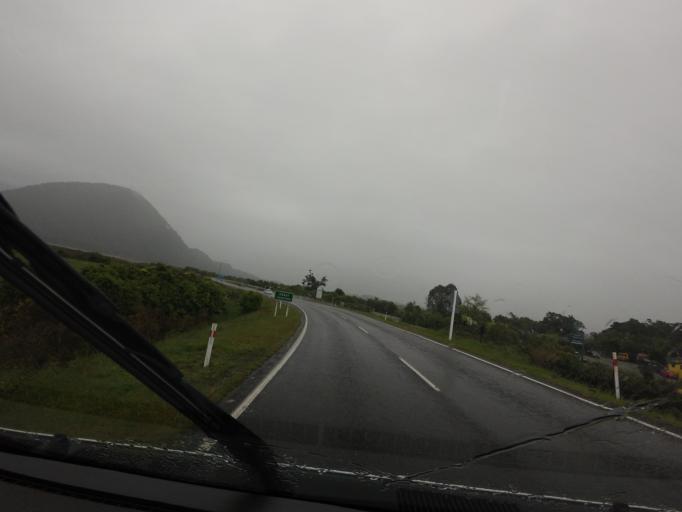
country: NZ
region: Otago
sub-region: Queenstown-Lakes District
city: Wanaka
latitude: -43.8583
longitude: 169.0421
